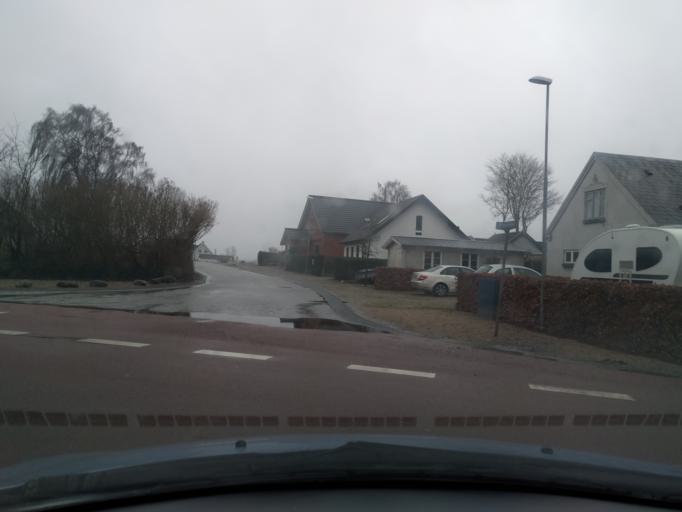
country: DK
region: South Denmark
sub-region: Odense Kommune
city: Bullerup
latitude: 55.3932
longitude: 10.5168
